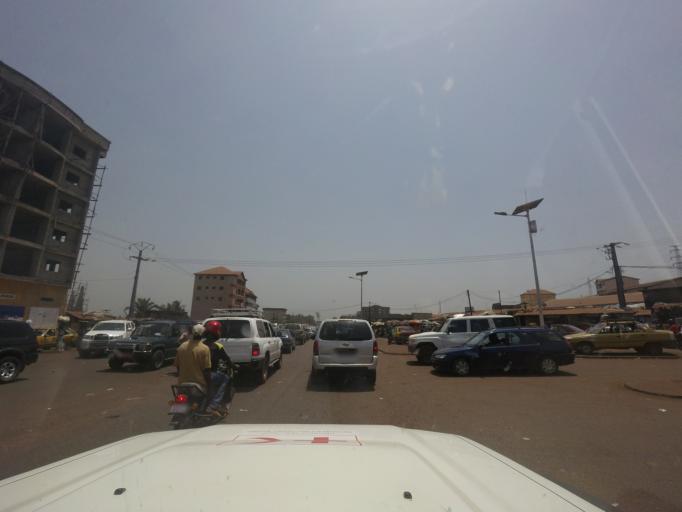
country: GN
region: Kindia
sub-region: Prefecture de Dubreka
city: Dubreka
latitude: 9.6445
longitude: -13.5625
